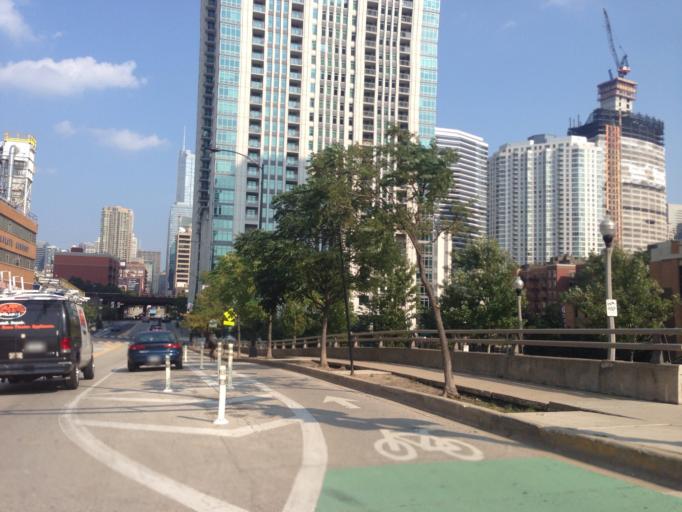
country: US
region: Illinois
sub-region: Cook County
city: Chicago
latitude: 41.8891
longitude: -87.6443
